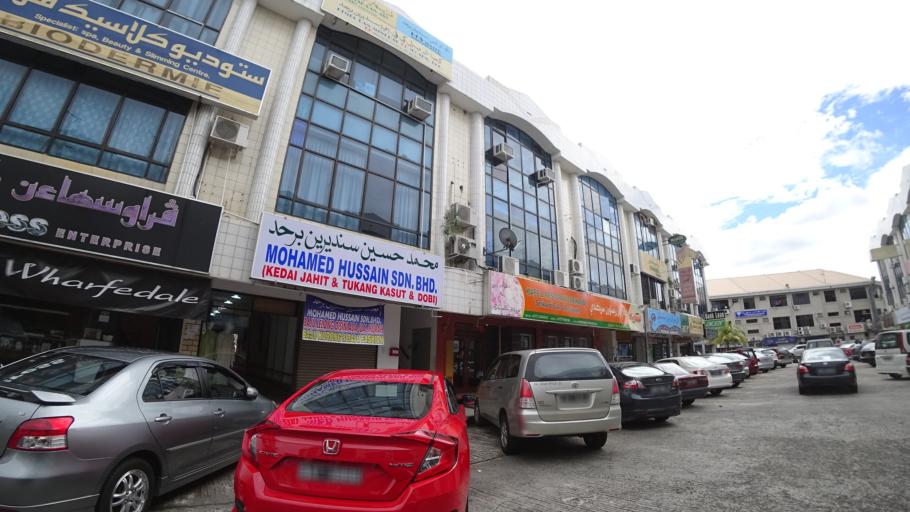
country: BN
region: Brunei and Muara
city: Bandar Seri Begawan
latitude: 4.9004
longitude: 114.9280
